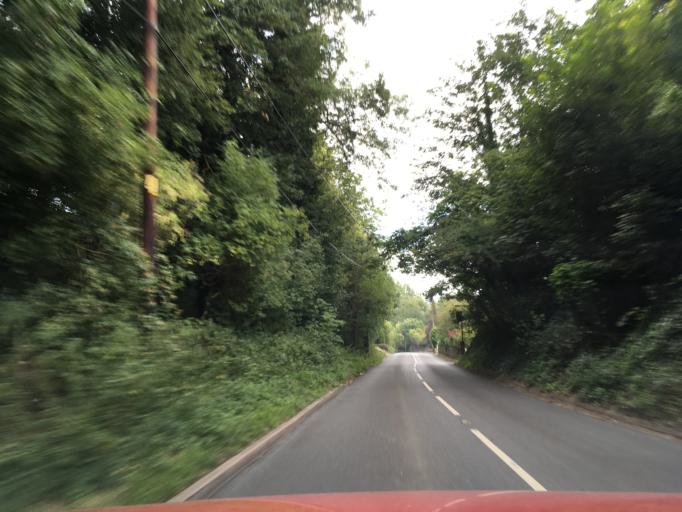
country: GB
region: England
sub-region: Kent
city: Yalding
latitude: 51.2329
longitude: 0.4354
